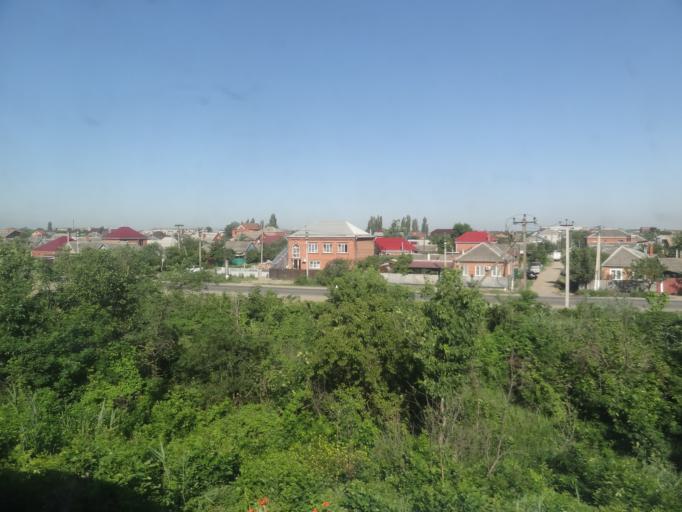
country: RU
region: Adygeya
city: Yablonovskiy
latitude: 44.9816
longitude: 38.9484
